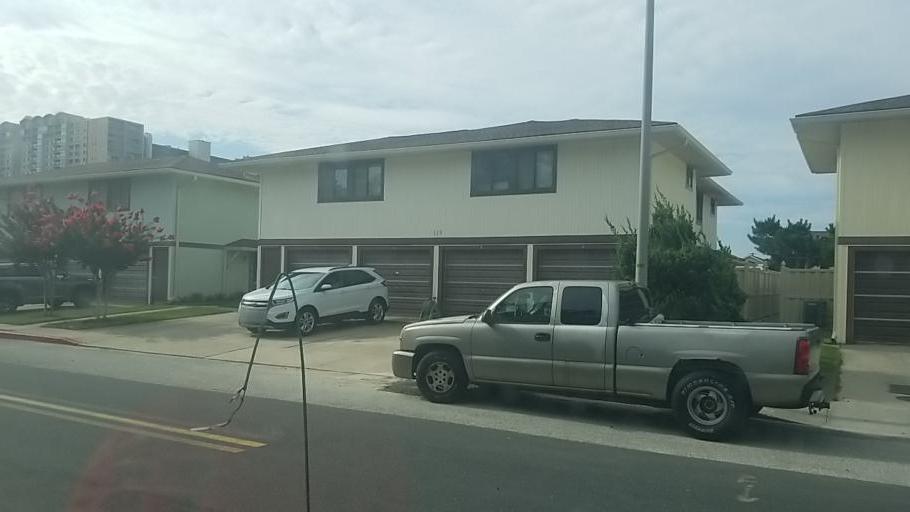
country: US
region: Maryland
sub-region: Worcester County
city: Ocean City
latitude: 38.4192
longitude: -75.0593
